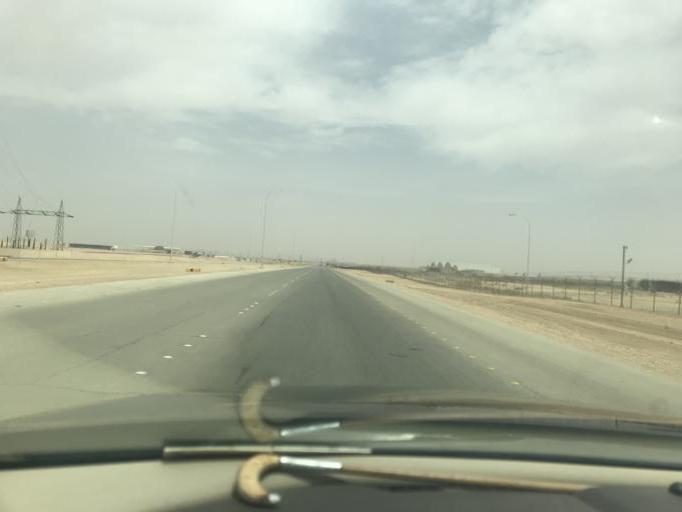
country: SA
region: Ar Riyad
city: Riyadh
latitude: 24.9515
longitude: 46.6753
